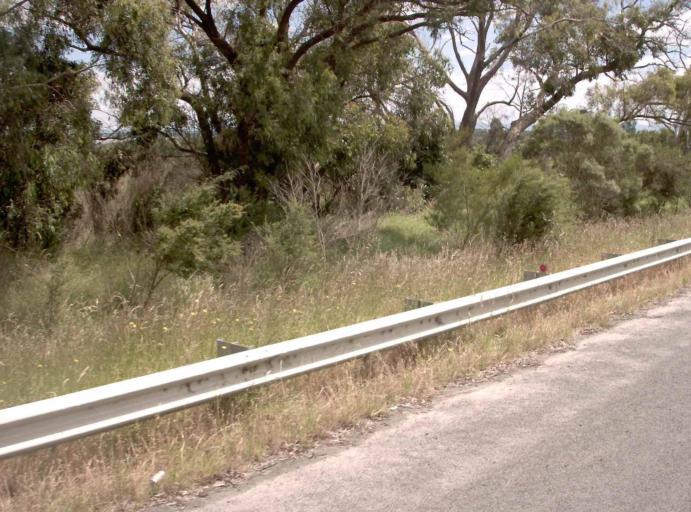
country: AU
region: Victoria
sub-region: Cardinia
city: Koo-Wee-Rup
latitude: -38.3784
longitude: 145.5567
